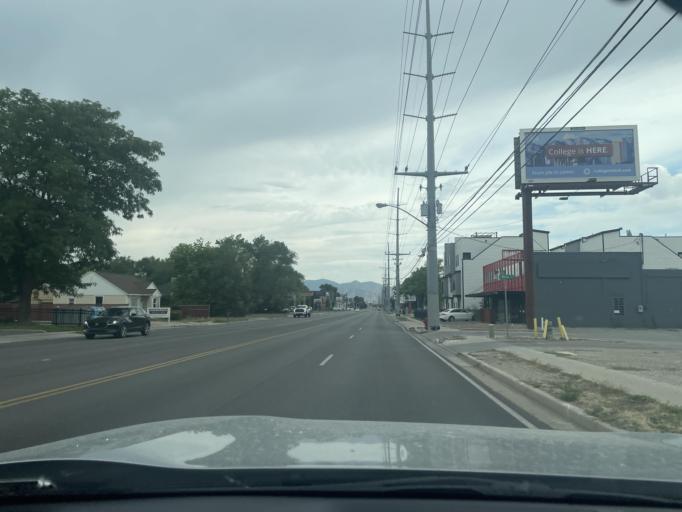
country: US
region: Utah
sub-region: Salt Lake County
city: Millcreek
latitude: 40.6871
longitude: -111.8777
